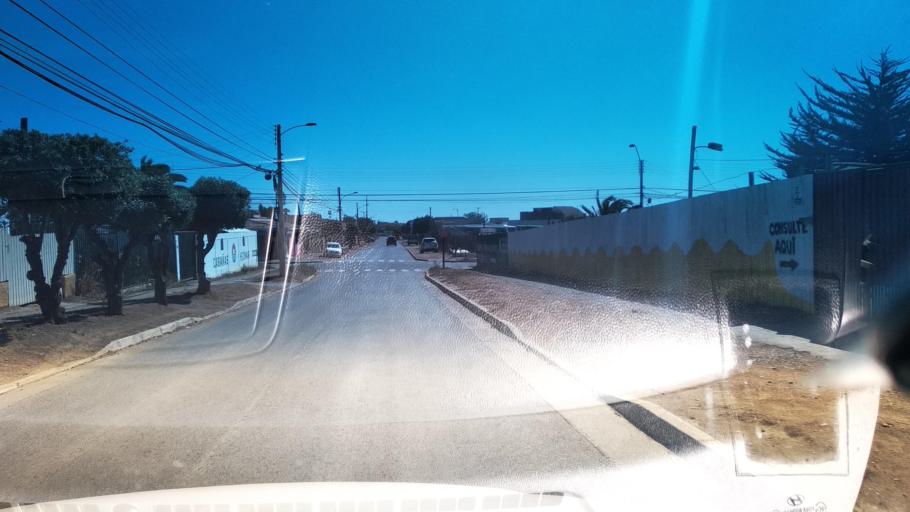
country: CL
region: O'Higgins
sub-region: Provincia de Colchagua
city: Santa Cruz
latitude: -34.3919
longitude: -72.0144
